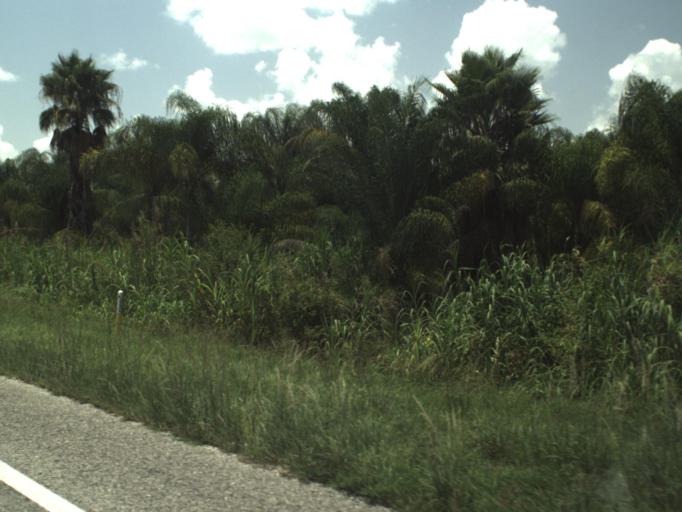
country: US
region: Florida
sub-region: Palm Beach County
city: South Bay
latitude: 26.6977
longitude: -80.7984
